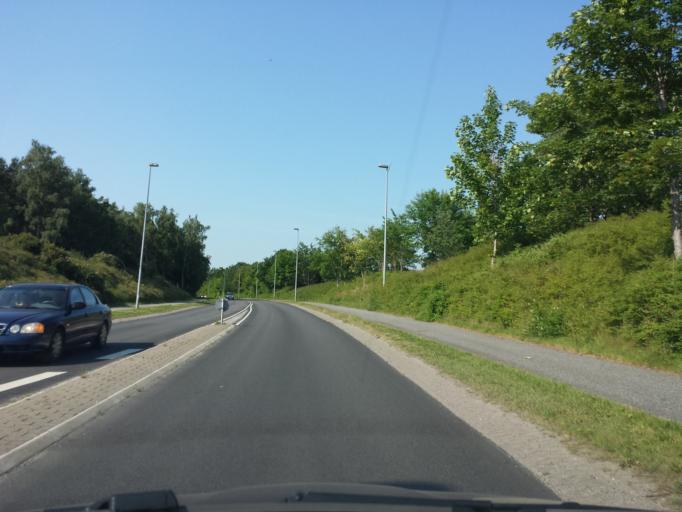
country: DK
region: Capital Region
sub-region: Egedal Kommune
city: Smorumnedre
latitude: 55.7391
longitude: 12.3146
